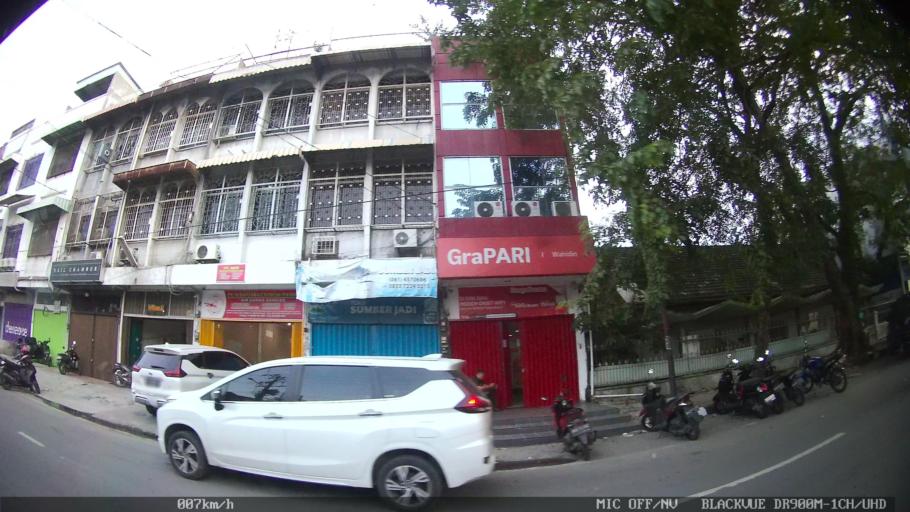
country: ID
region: North Sumatra
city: Medan
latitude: 3.5876
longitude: 98.6939
